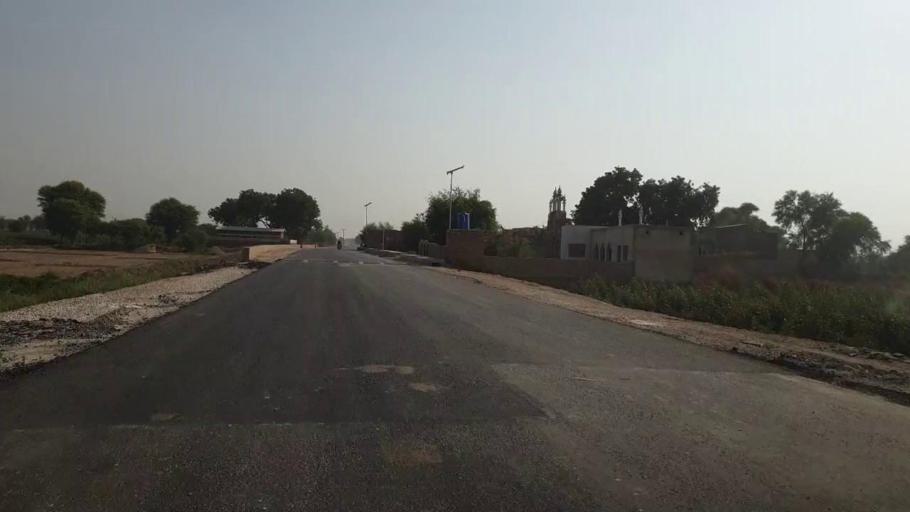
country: PK
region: Sindh
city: Bhan
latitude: 26.5364
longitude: 67.7882
